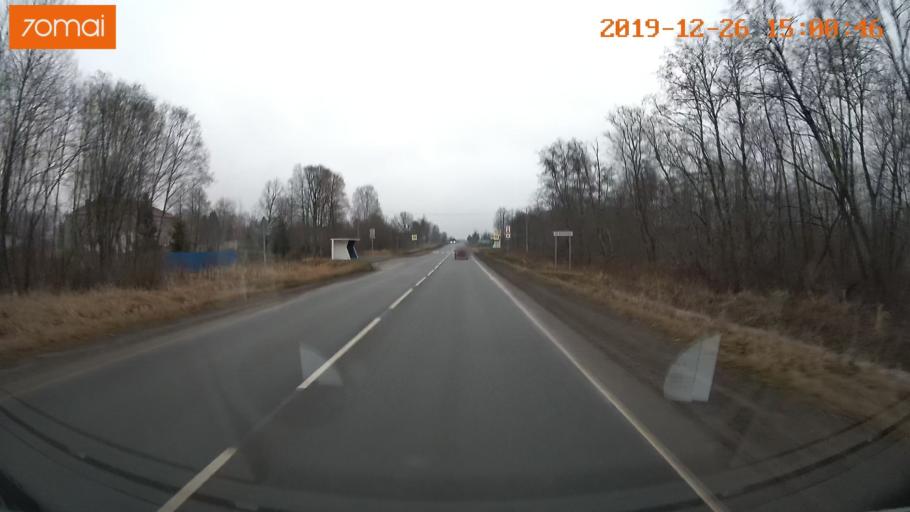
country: RU
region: Jaroslavl
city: Rybinsk
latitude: 58.2431
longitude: 38.8565
